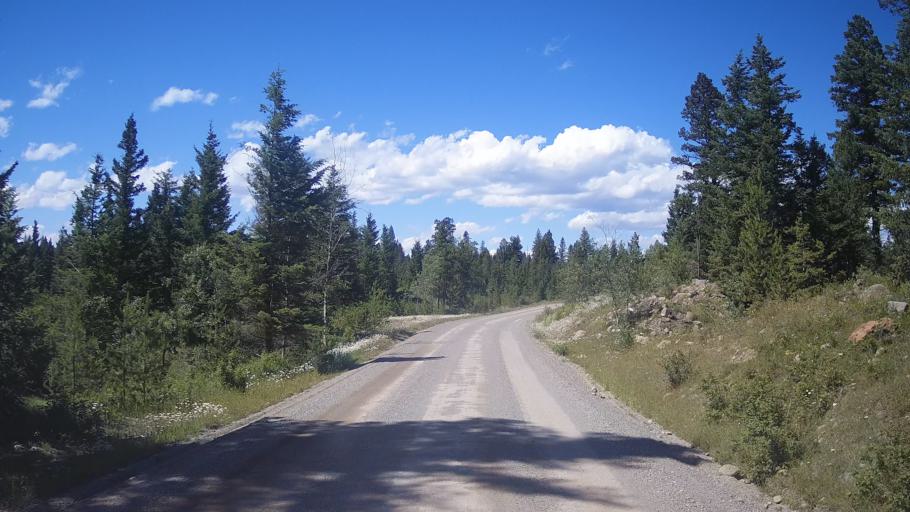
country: CA
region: British Columbia
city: Cache Creek
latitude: 51.1598
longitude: -121.5541
